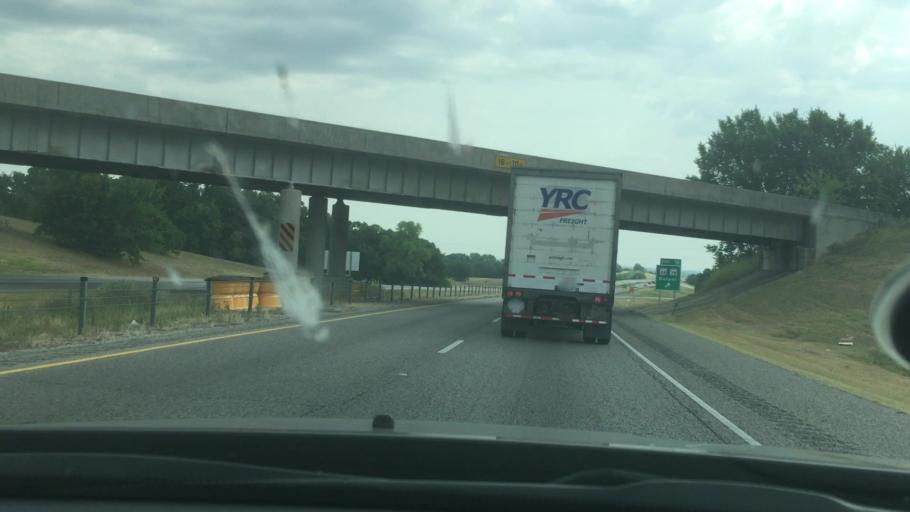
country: US
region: Oklahoma
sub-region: Bryan County
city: Durant
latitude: 34.0335
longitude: -96.3802
